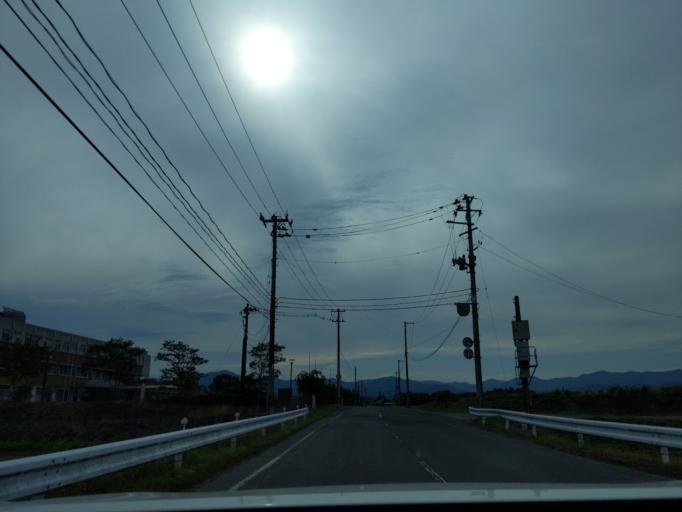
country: JP
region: Fukushima
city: Koriyama
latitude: 37.3759
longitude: 140.3185
